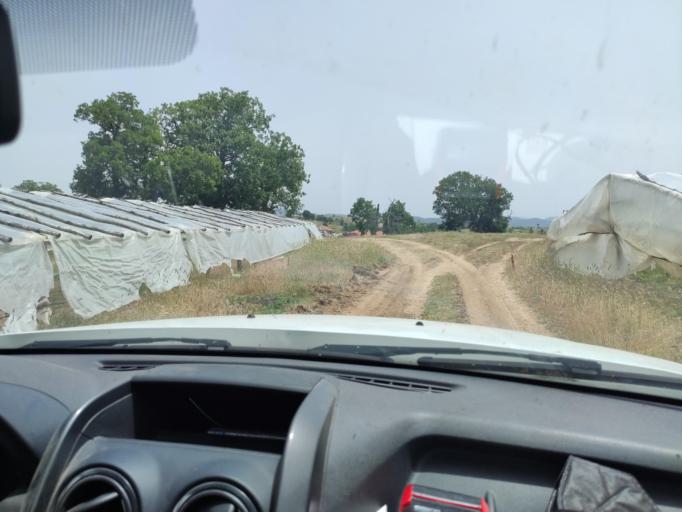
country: MK
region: Radovis
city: Radovish
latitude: 41.6785
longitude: 22.4008
